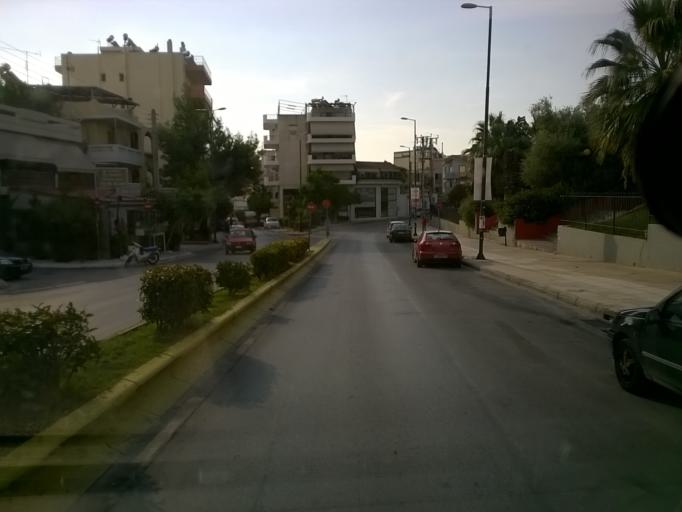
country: GR
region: Attica
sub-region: Nomarchia Athinas
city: Agios Dimitrios
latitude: 37.9340
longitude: 23.7235
